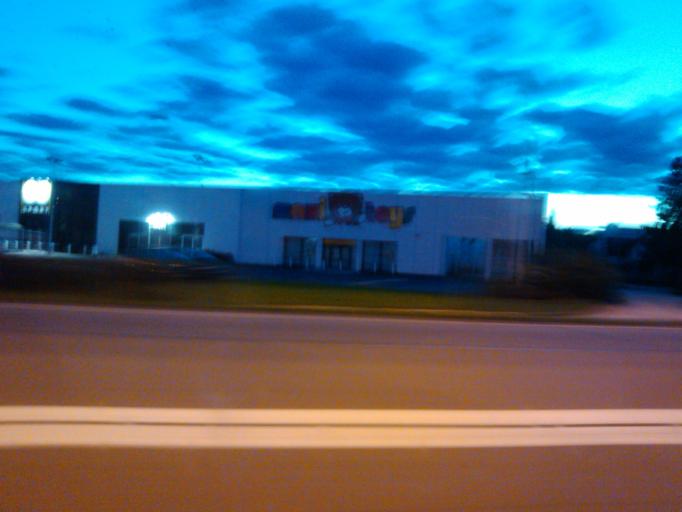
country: FR
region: Bourgogne
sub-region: Departement de Saone-et-Loire
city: Champforgeuil
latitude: 46.7987
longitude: 4.8348
